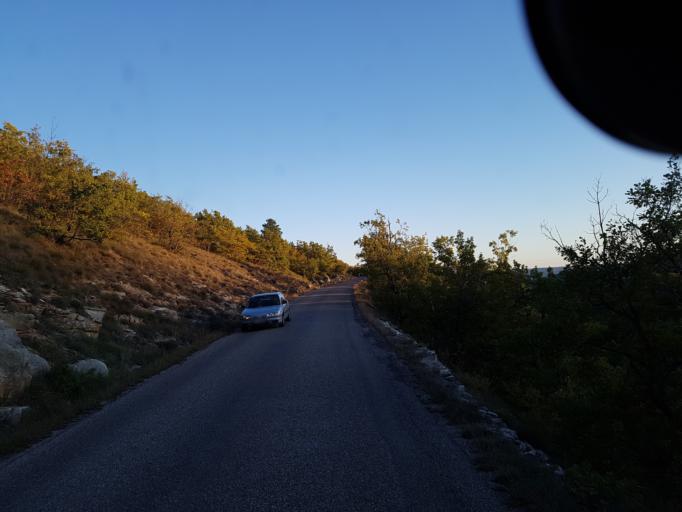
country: FR
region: Provence-Alpes-Cote d'Azur
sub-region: Departement des Alpes-de-Haute-Provence
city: Peyruis
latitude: 44.0773
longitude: 5.9199
